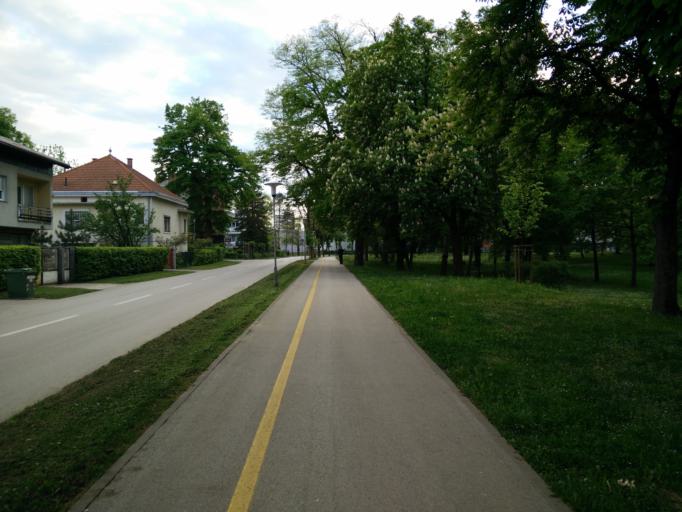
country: HR
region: Karlovacka
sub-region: Grad Karlovac
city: Karlovac
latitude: 45.4906
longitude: 15.5604
